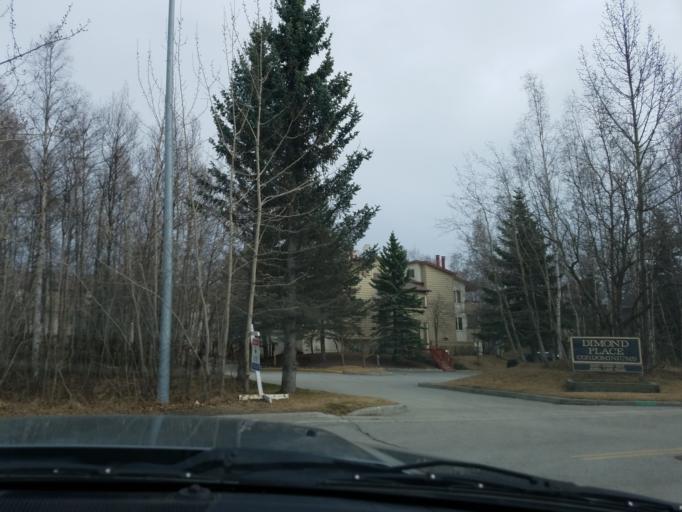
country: US
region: Alaska
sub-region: Anchorage Municipality
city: Anchorage
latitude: 61.1360
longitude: -149.9520
